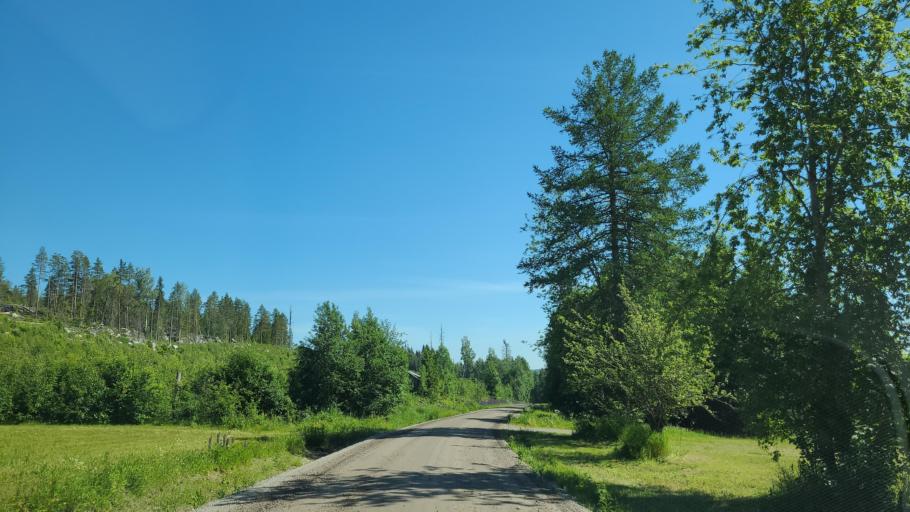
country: SE
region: Vaesterbotten
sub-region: Bjurholms Kommun
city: Bjurholm
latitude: 63.6752
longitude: 19.0519
